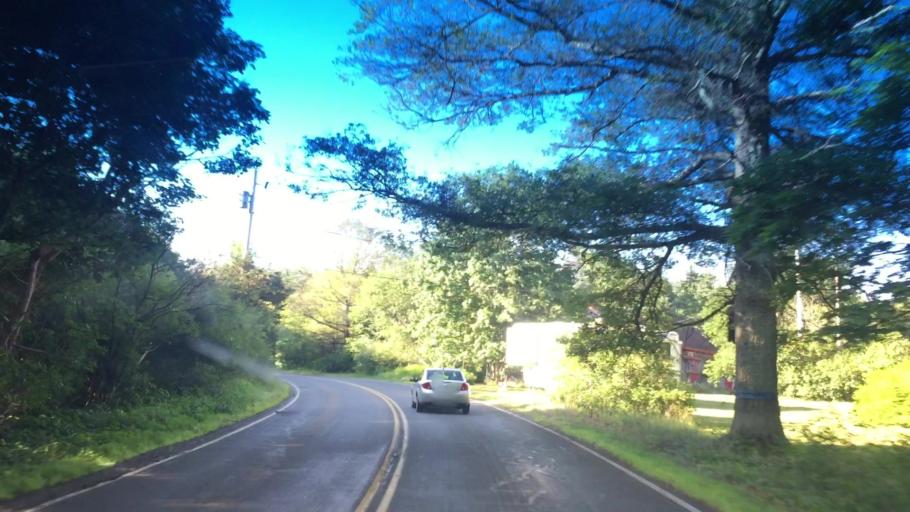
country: US
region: Massachusetts
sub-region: Norfolk County
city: Millis-Clicquot
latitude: 42.1415
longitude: -71.3491
